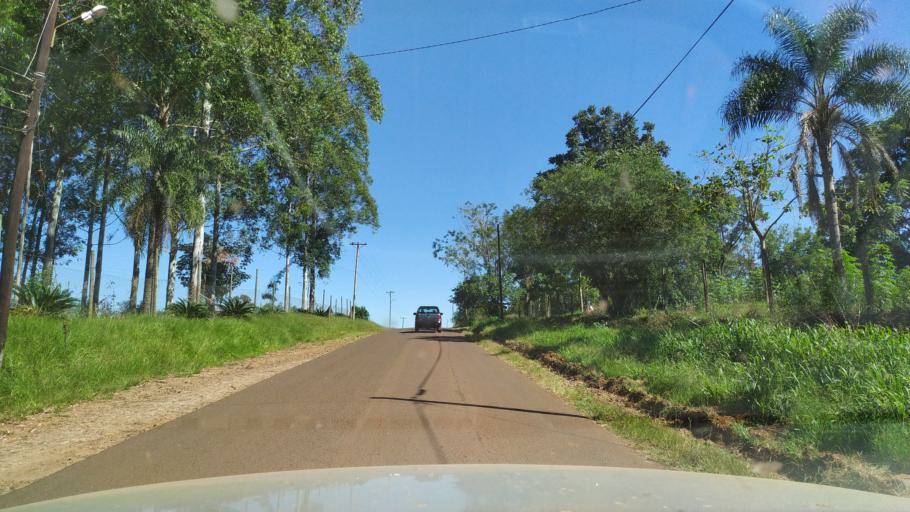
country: AR
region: Misiones
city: Caraguatay
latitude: -26.6477
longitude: -54.7477
